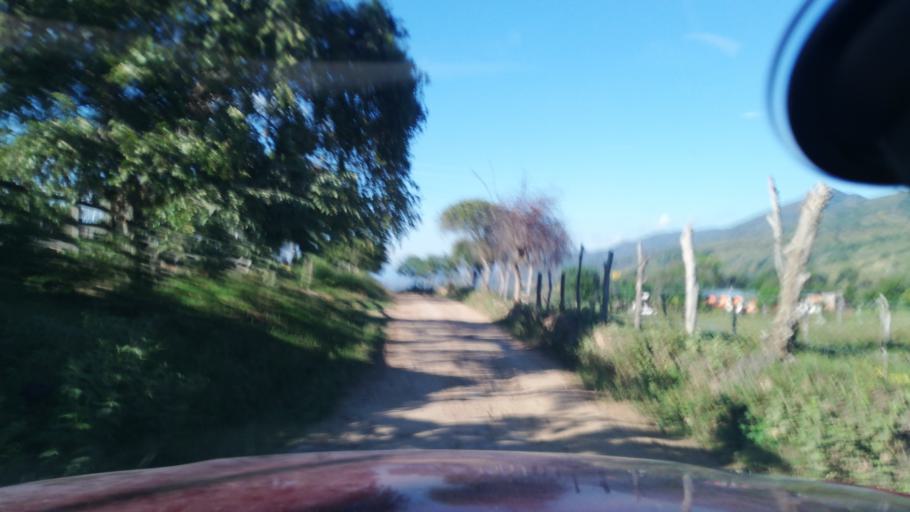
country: CO
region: Cundinamarca
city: Viani
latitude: 4.8115
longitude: -74.6203
